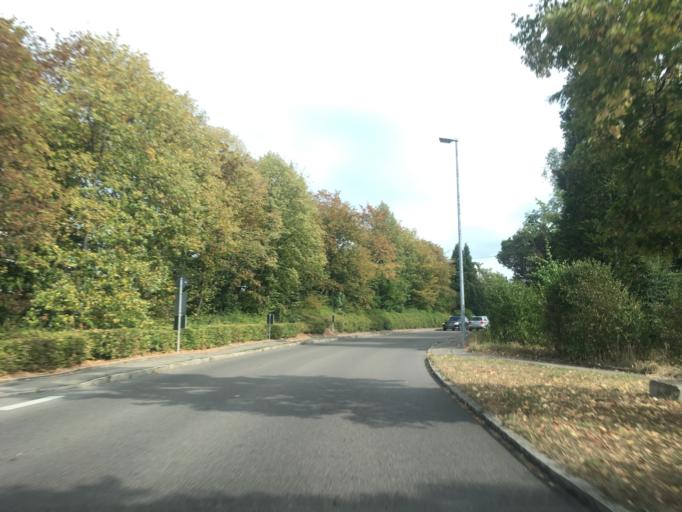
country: DE
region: Baden-Wuerttemberg
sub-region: Tuebingen Region
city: Wannweil
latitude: 48.4780
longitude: 9.1454
